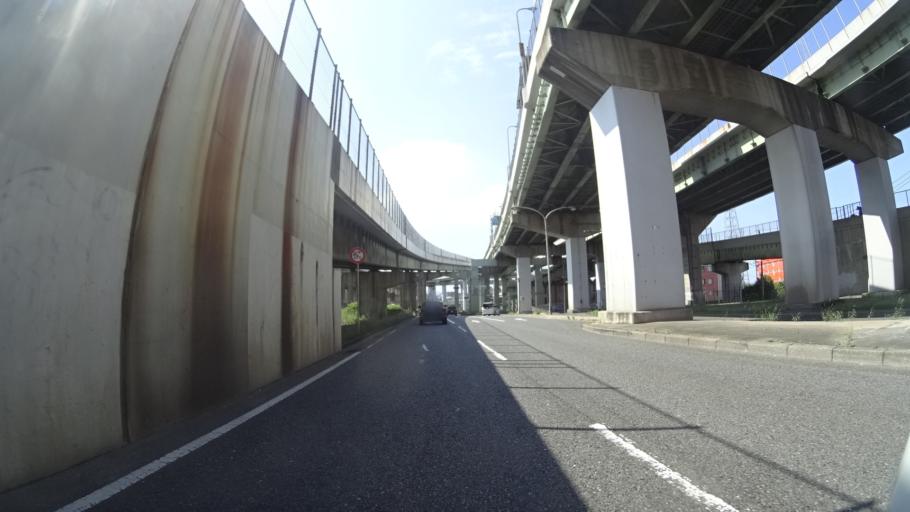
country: JP
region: Fukuoka
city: Kitakyushu
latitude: 33.8895
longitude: 130.8723
